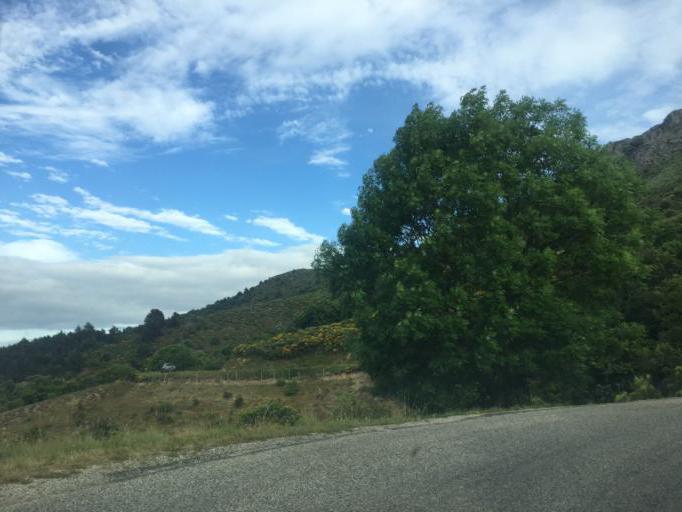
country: FR
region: Rhone-Alpes
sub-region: Departement de l'Ardeche
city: Flaviac
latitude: 44.7946
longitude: 4.6695
